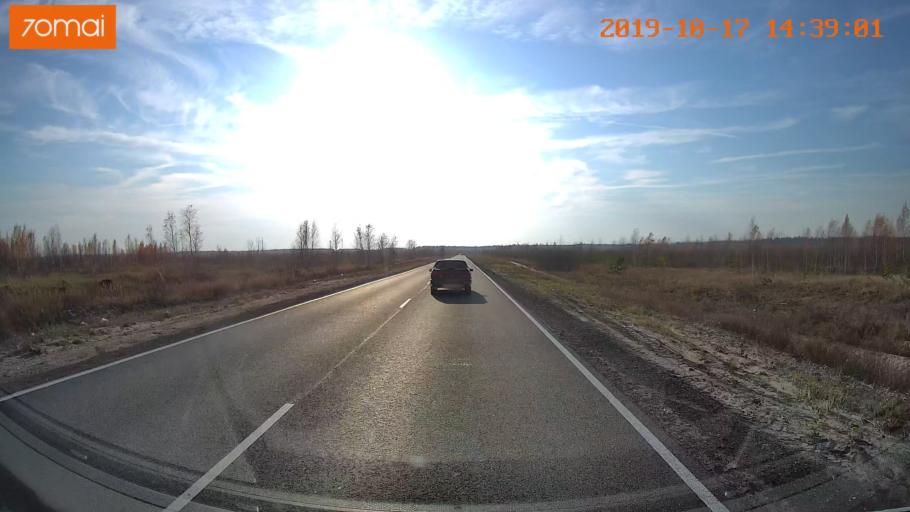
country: RU
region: Rjazan
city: Solotcha
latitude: 54.8652
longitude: 39.9782
